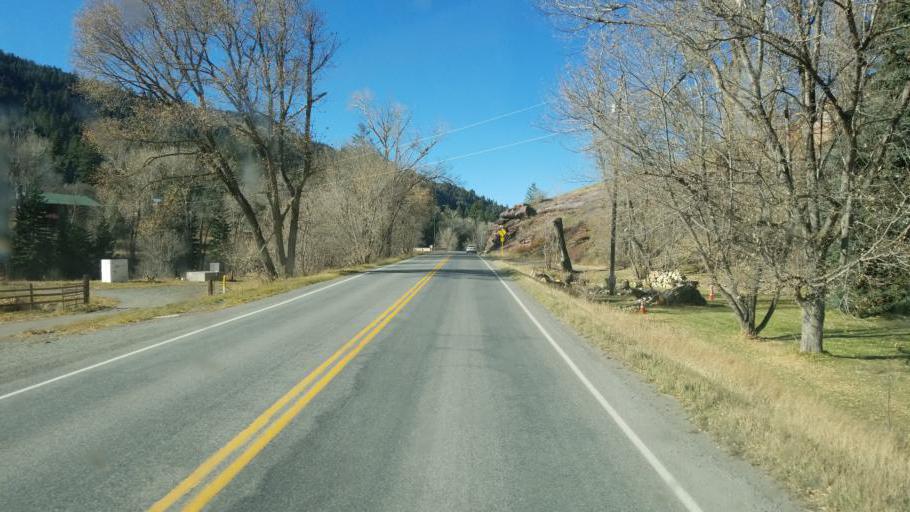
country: US
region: Colorado
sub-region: Ouray County
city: Ouray
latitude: 38.0516
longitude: -107.6856
